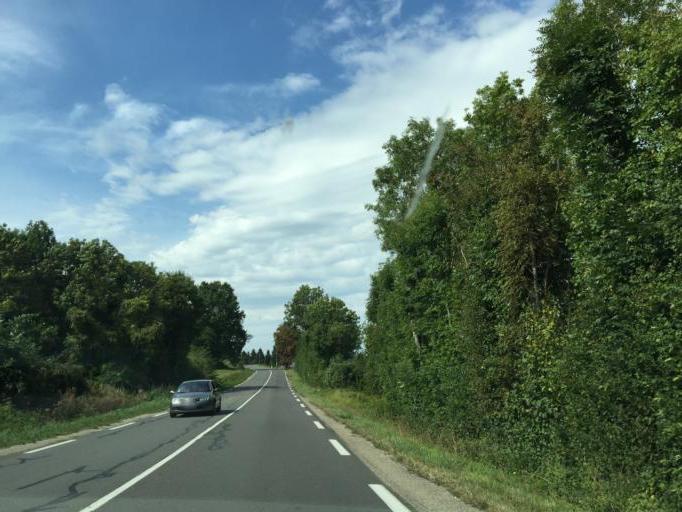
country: FR
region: Rhone-Alpes
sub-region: Departement de l'Isere
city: Saint-Andre-le-Gaz
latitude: 45.5469
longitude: 5.5150
